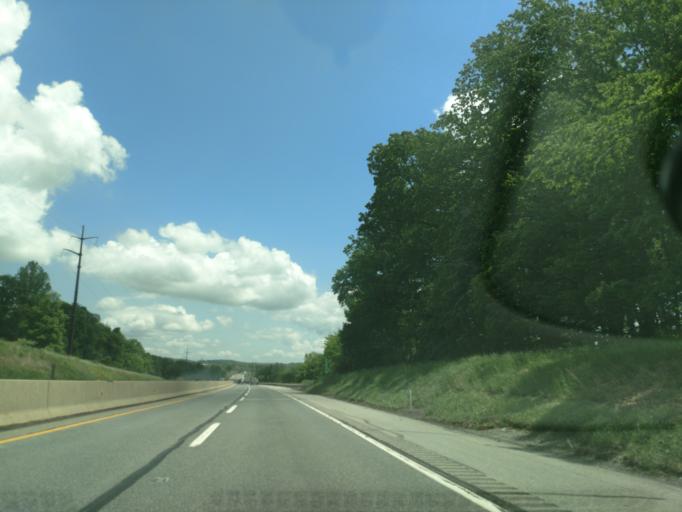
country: US
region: Pennsylvania
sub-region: Lancaster County
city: Reamstown
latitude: 40.2272
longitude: -76.1123
